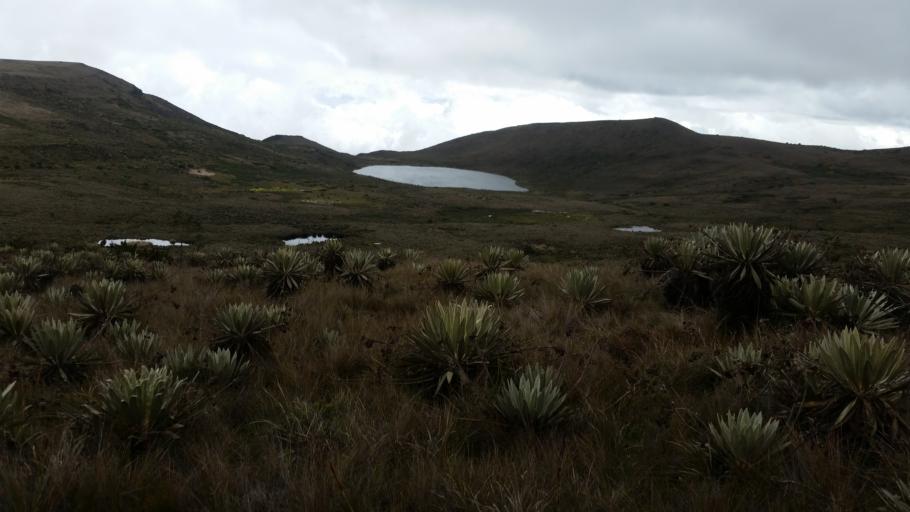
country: CO
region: Cundinamarca
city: Pasca
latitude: 4.3689
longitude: -74.2181
